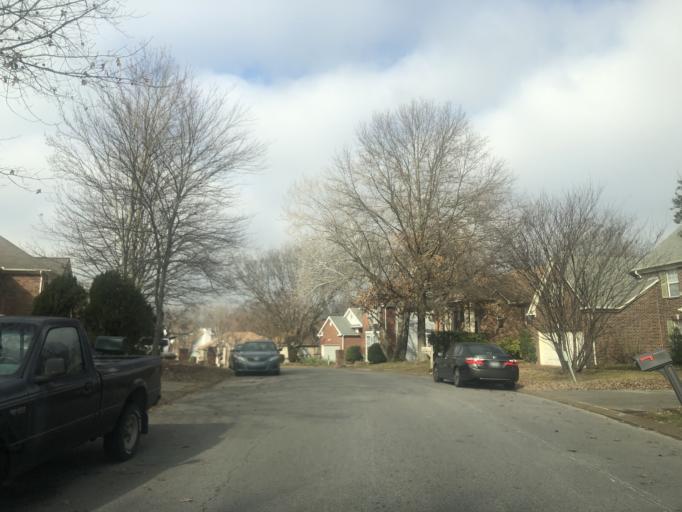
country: US
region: Tennessee
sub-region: Rutherford County
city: La Vergne
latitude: 36.0848
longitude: -86.6565
